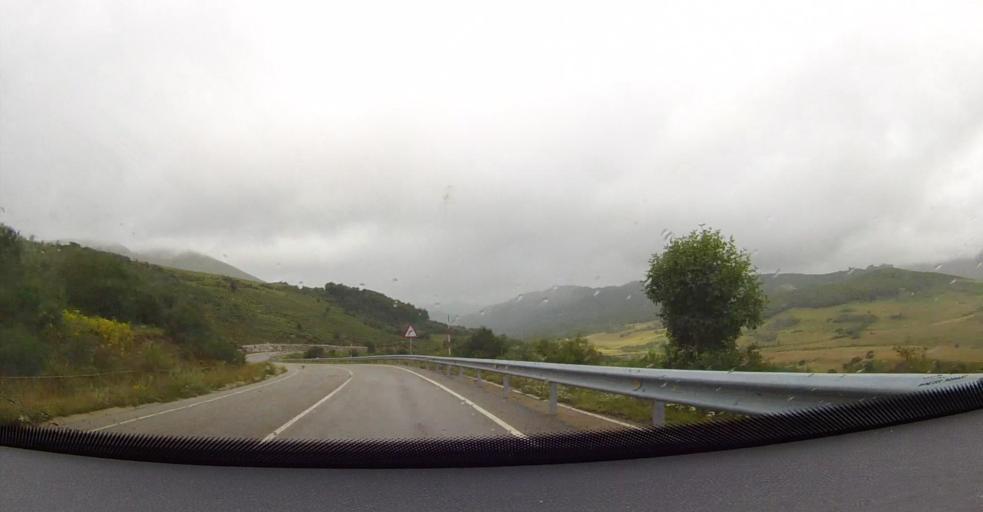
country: ES
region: Castille and Leon
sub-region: Provincia de Leon
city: Marana
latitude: 43.0728
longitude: -5.2083
